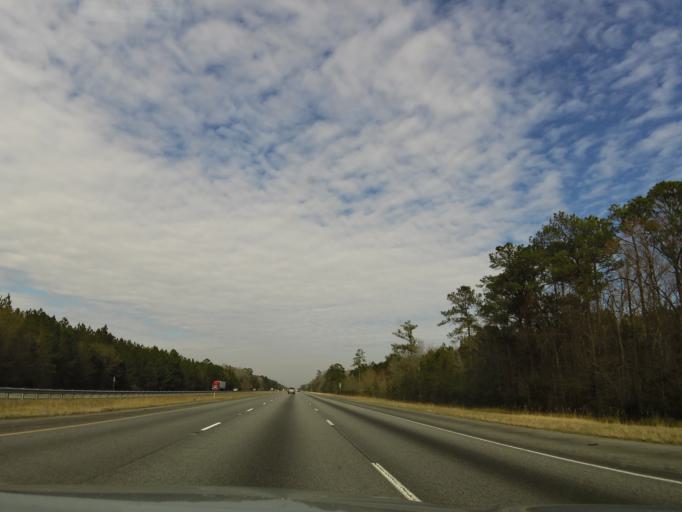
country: US
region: Georgia
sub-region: McIntosh County
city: Darien
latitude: 31.5829
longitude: -81.4300
